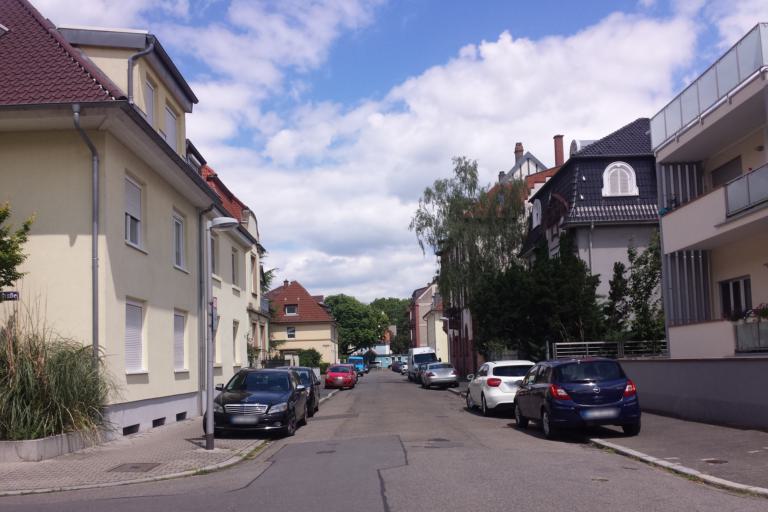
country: DE
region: Baden-Wuerttemberg
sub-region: Karlsruhe Region
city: Mannheim
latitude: 49.5095
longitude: 8.5096
